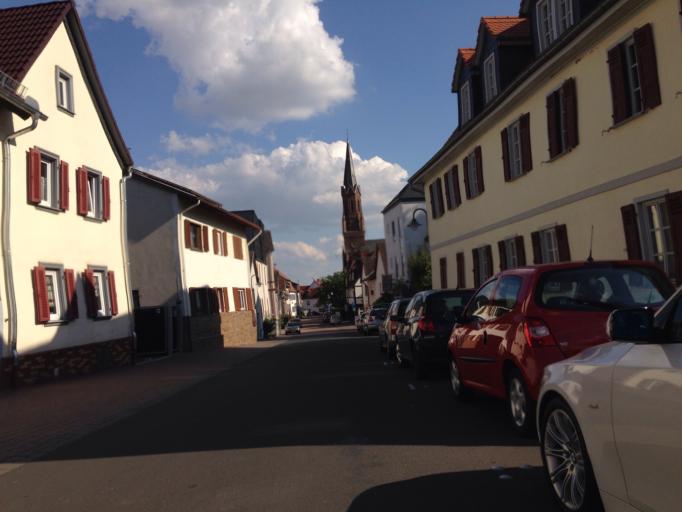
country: DE
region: Hesse
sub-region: Regierungsbezirk Darmstadt
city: Friedrichsdorf
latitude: 50.2446
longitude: 8.6499
